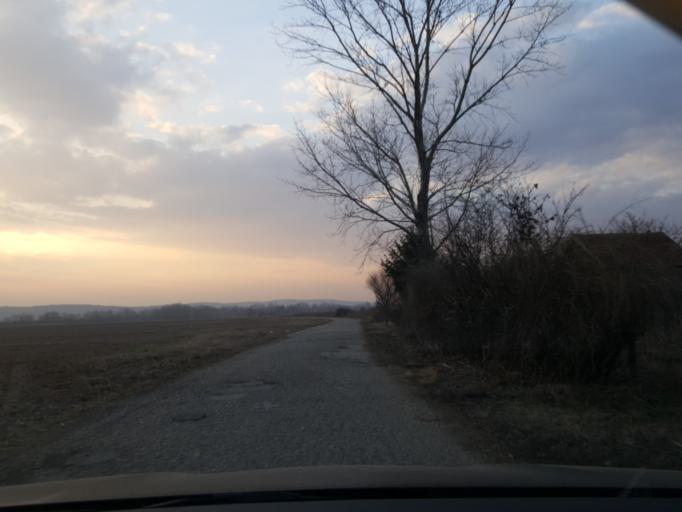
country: RS
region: Central Serbia
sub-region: Nisavski Okrug
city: Aleksinac
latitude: 43.5518
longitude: 21.6669
